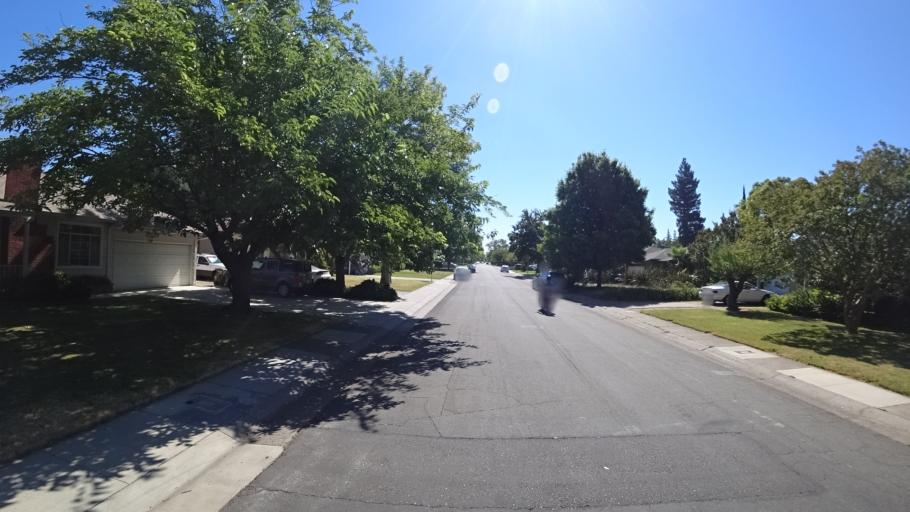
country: US
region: California
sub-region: Sacramento County
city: Parkway
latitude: 38.5284
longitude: -121.4936
